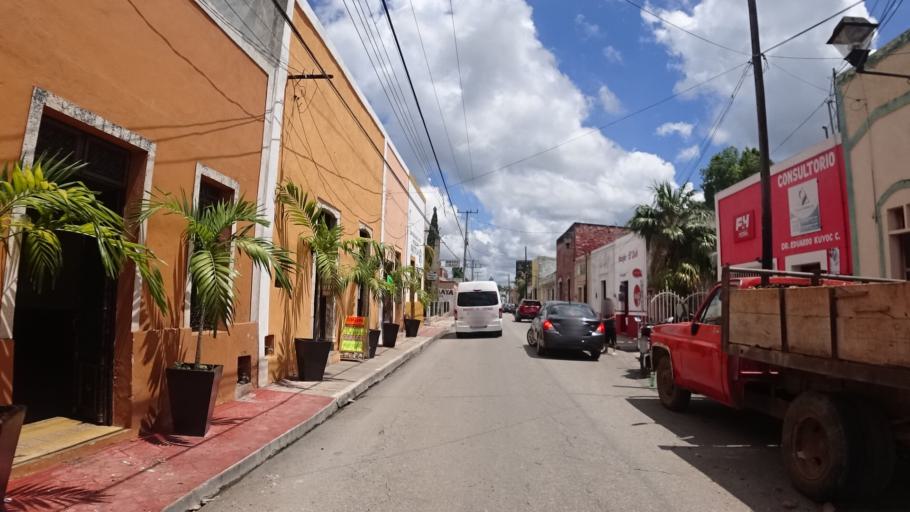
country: MX
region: Yucatan
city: Valladolid
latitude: 20.6898
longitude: -88.2081
